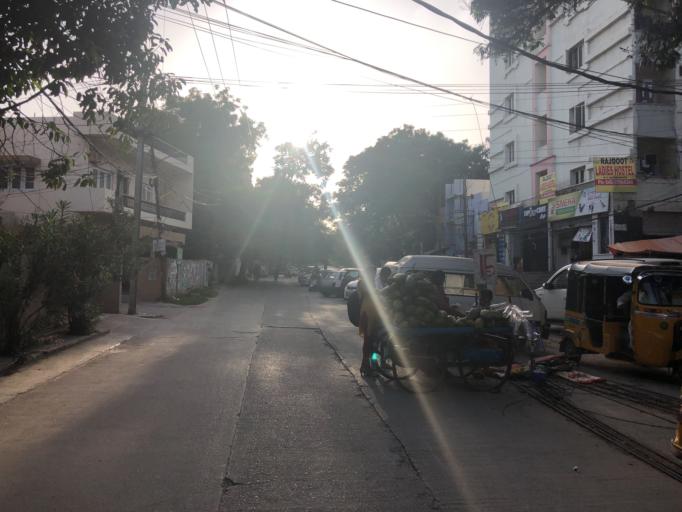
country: IN
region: Telangana
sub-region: Rangareddi
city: Kukatpalli
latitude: 17.4389
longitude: 78.4391
